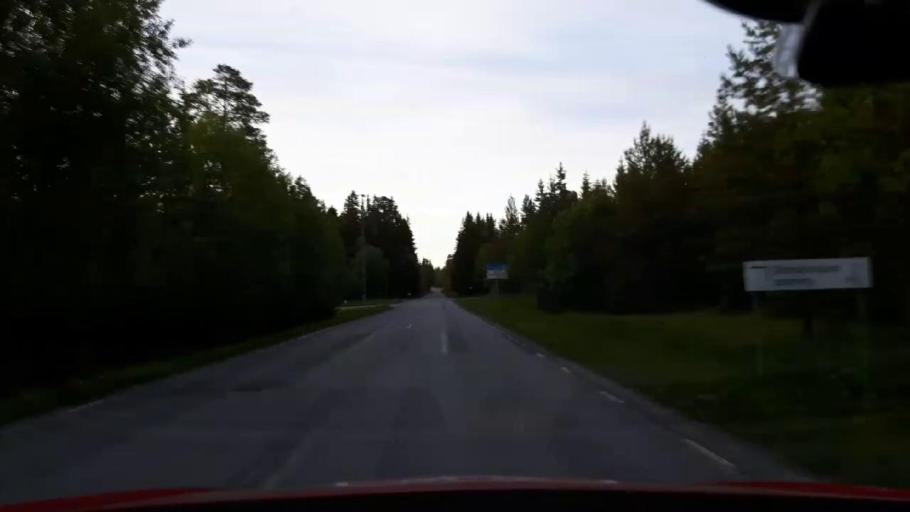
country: SE
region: Jaemtland
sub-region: OEstersunds Kommun
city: Ostersund
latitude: 63.1251
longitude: 14.4426
